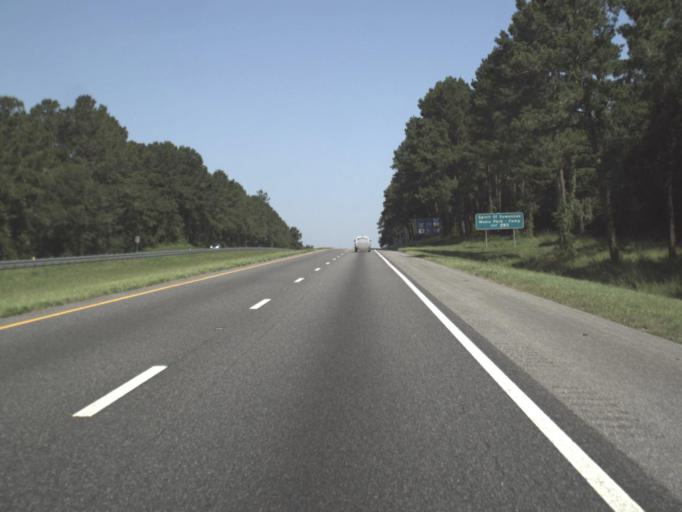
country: US
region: Florida
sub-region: Suwannee County
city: Live Oak
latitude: 30.3248
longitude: -82.9543
